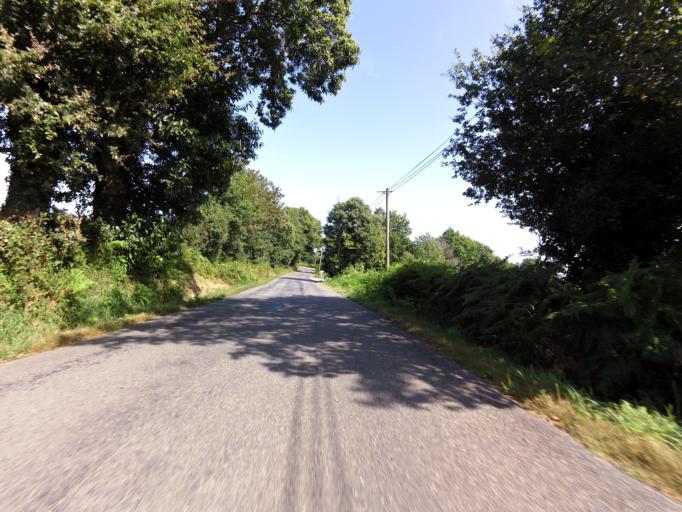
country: FR
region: Brittany
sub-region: Departement du Morbihan
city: Limerzel
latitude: 47.6570
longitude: -2.3973
